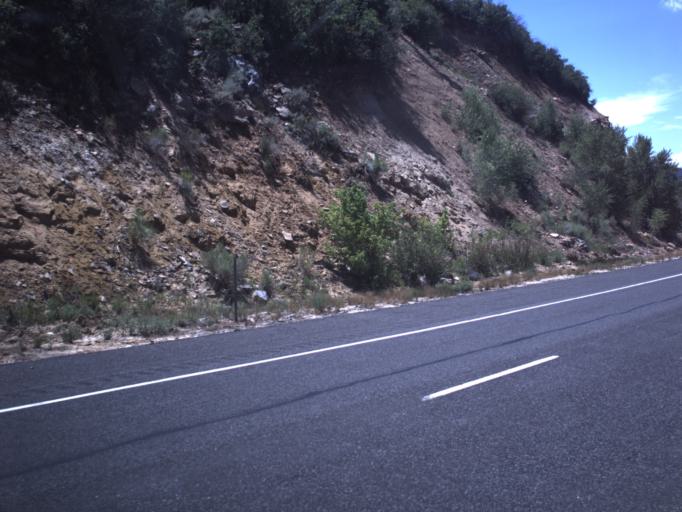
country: US
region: Utah
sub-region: Kane County
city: Kanab
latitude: 37.3897
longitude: -112.5662
